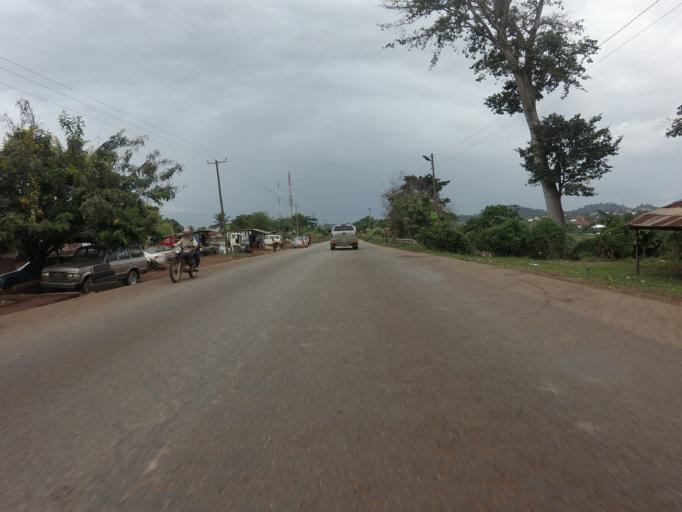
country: GH
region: Ashanti
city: Konongo
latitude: 6.6236
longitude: -1.2028
